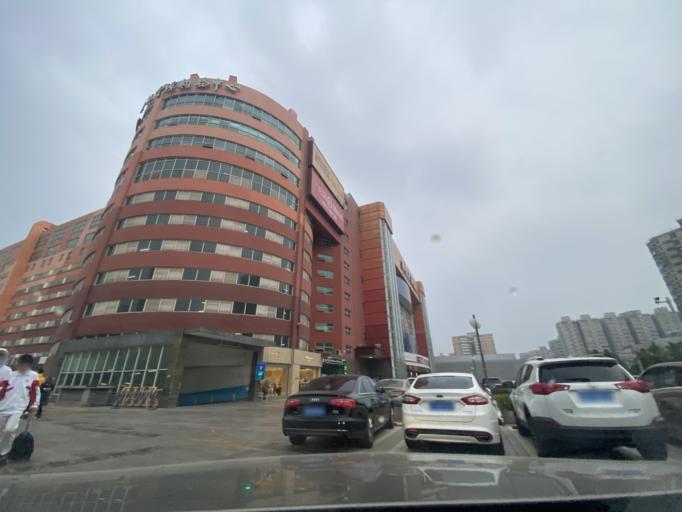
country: CN
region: Beijing
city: Sijiqing
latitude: 39.9580
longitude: 116.2788
